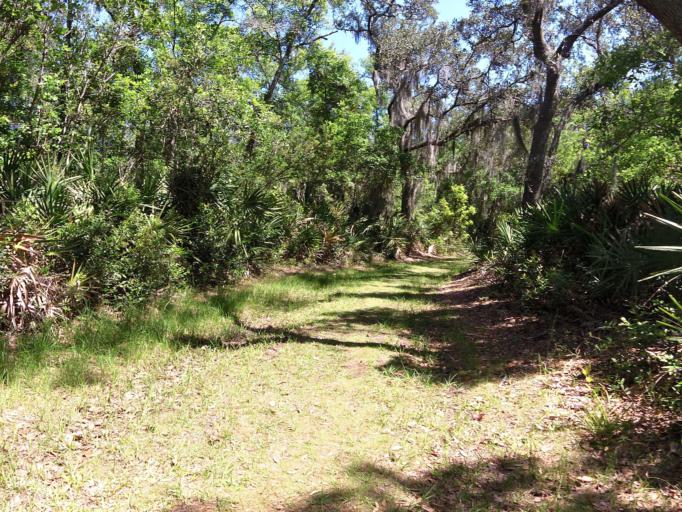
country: US
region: Florida
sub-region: Duval County
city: Atlantic Beach
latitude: 30.4467
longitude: -81.4823
